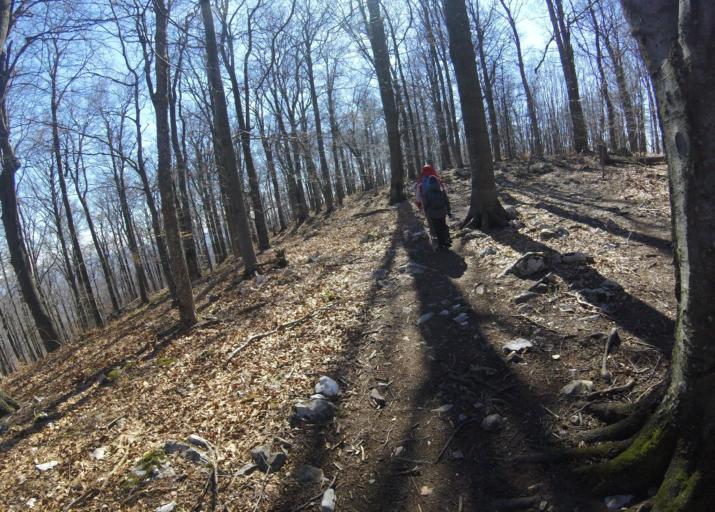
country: HU
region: Heves
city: Szilvasvarad
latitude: 48.0586
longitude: 20.4603
